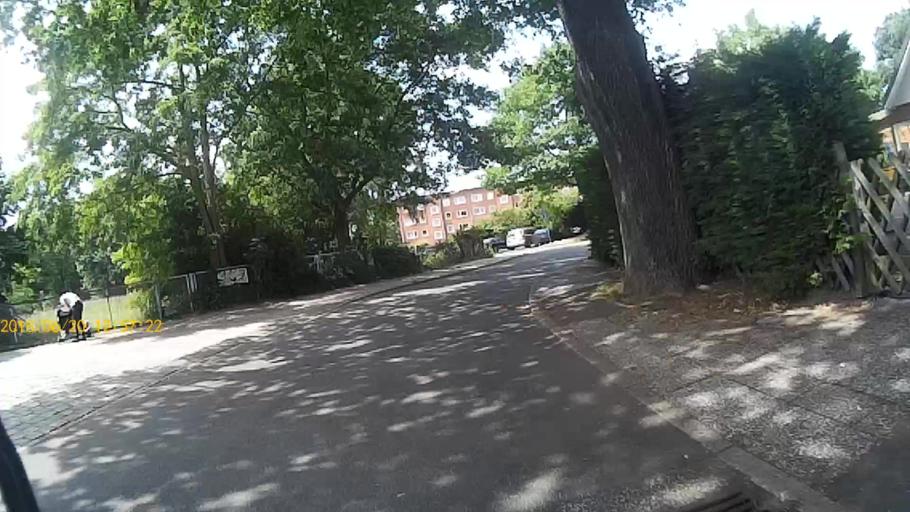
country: DE
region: Lower Saxony
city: Neu Wulmstorf
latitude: 53.4743
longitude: 9.8623
